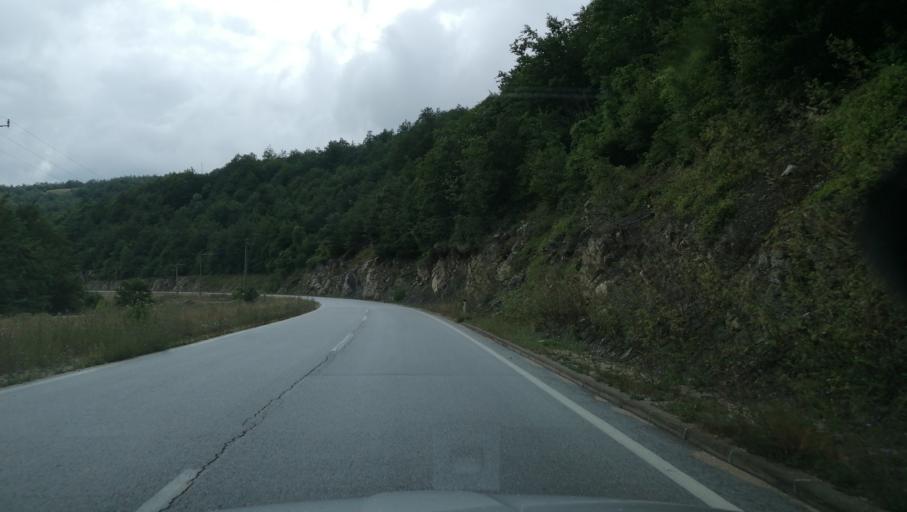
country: BA
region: Republika Srpska
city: Gacko
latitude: 43.2324
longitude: 18.5885
